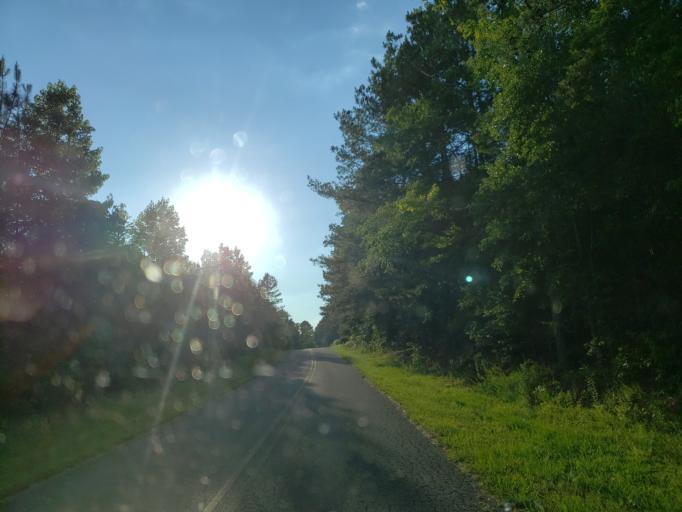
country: US
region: Georgia
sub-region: Haralson County
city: Tallapoosa
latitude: 33.8308
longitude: -85.2809
